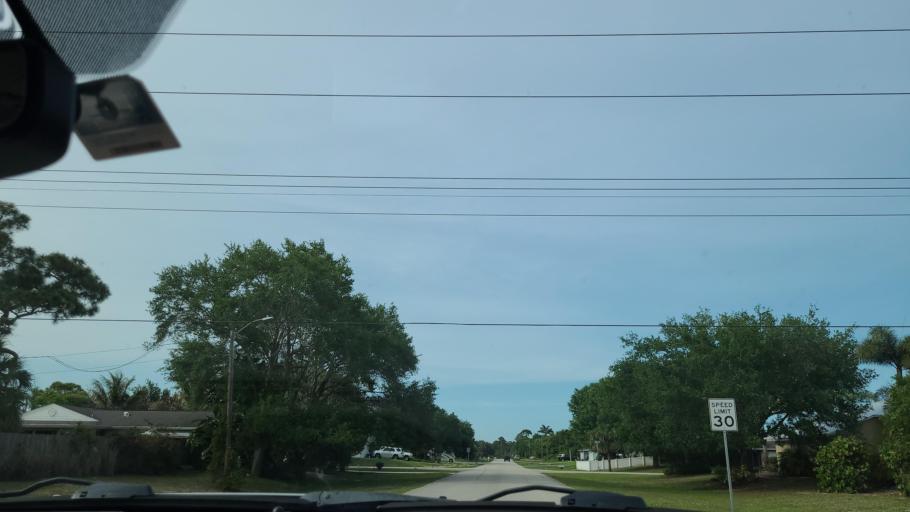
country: US
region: Florida
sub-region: Indian River County
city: Sebastian
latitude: 27.7995
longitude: -80.4717
